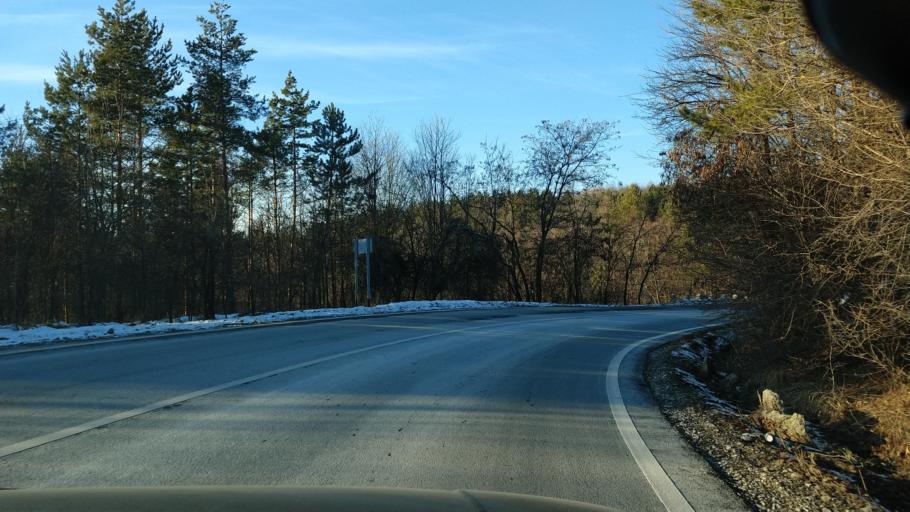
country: RO
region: Bacau
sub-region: Comuna Luizi-Calugara
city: Luizi-Calugara
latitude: 46.4987
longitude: 26.8024
